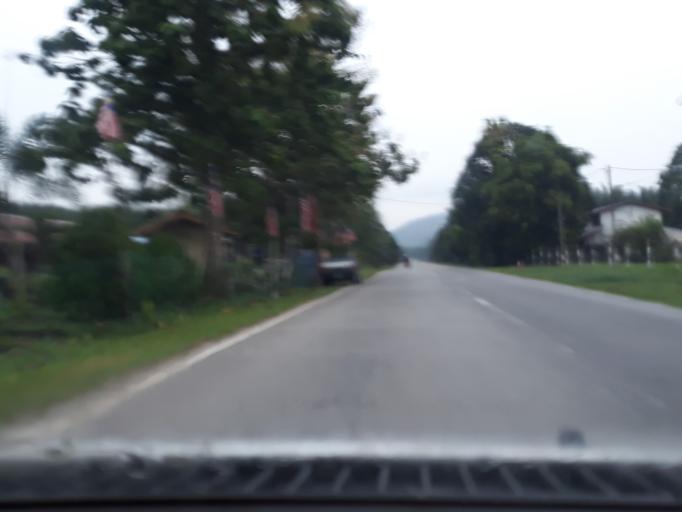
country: MY
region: Kedah
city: Kulim
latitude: 5.2527
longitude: 100.6033
